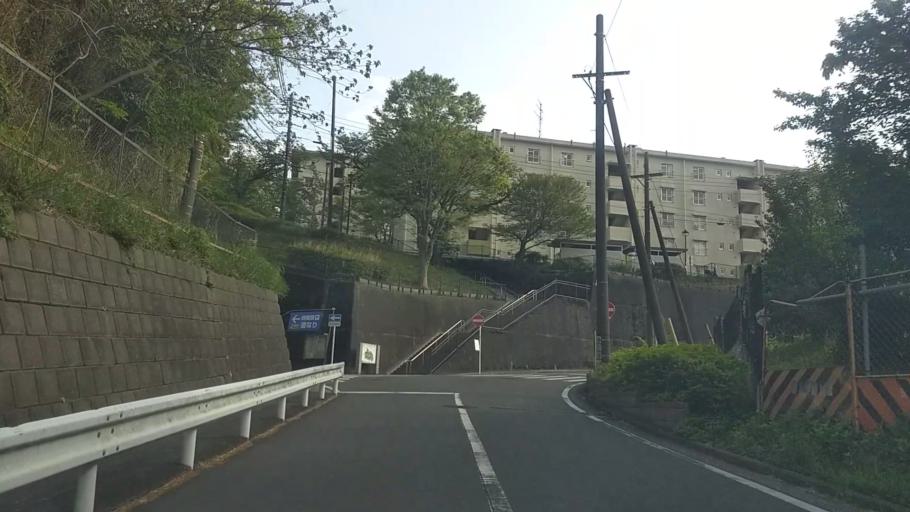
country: JP
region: Kanagawa
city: Kamakura
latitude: 35.3606
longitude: 139.5567
